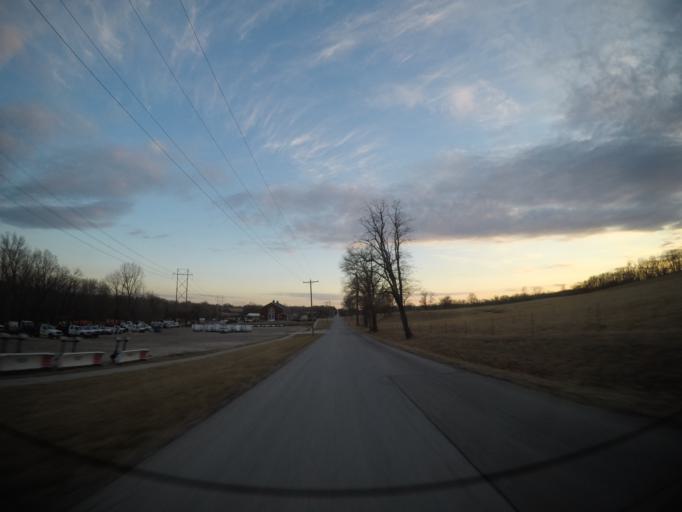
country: US
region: Kansas
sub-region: Wyandotte County
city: Bonner Springs
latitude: 39.0560
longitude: -94.9088
